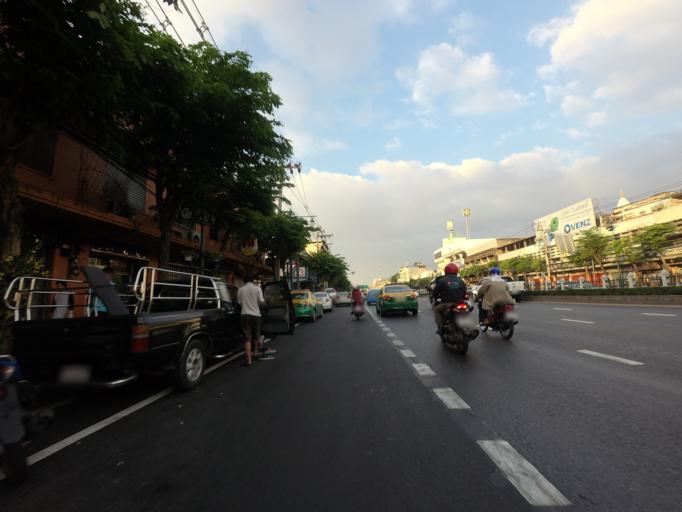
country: TH
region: Bangkok
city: Thon Buri
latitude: 13.7316
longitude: 100.4948
